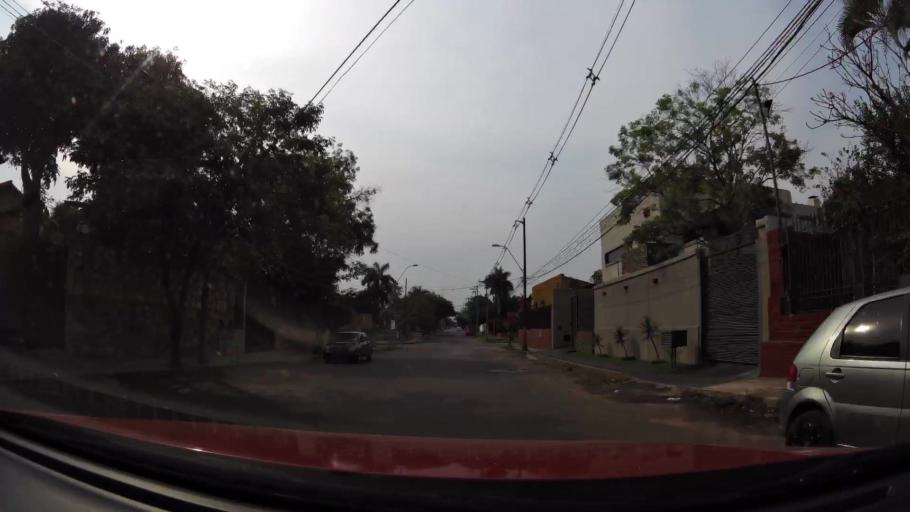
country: PY
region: Asuncion
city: Asuncion
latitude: -25.2631
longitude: -57.5788
